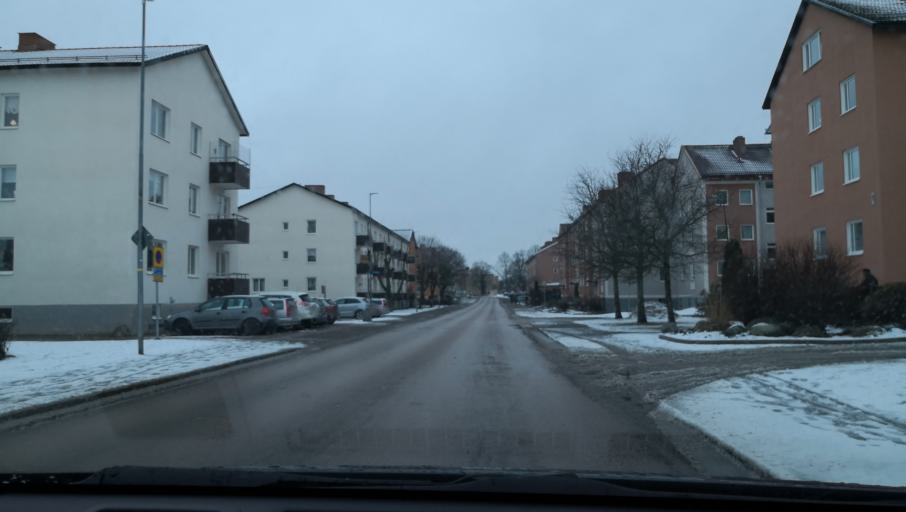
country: SE
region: Vaestmanland
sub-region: Kopings Kommun
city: Koping
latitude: 59.5239
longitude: 15.9885
